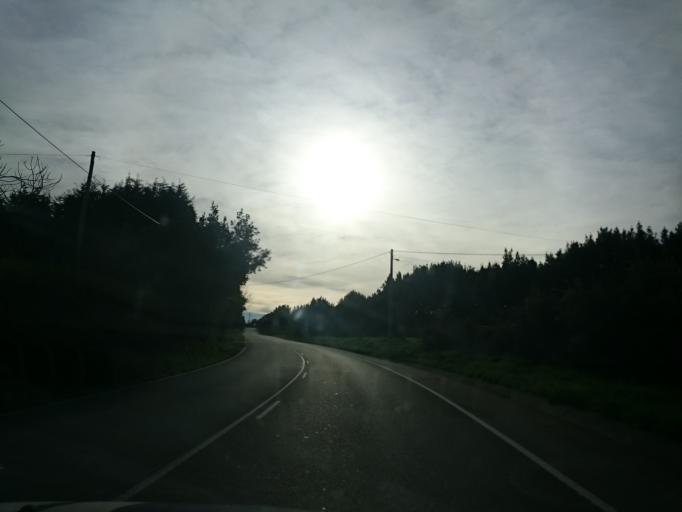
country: ES
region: Asturias
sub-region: Province of Asturias
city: Arriba
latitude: 43.5150
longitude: -5.5977
